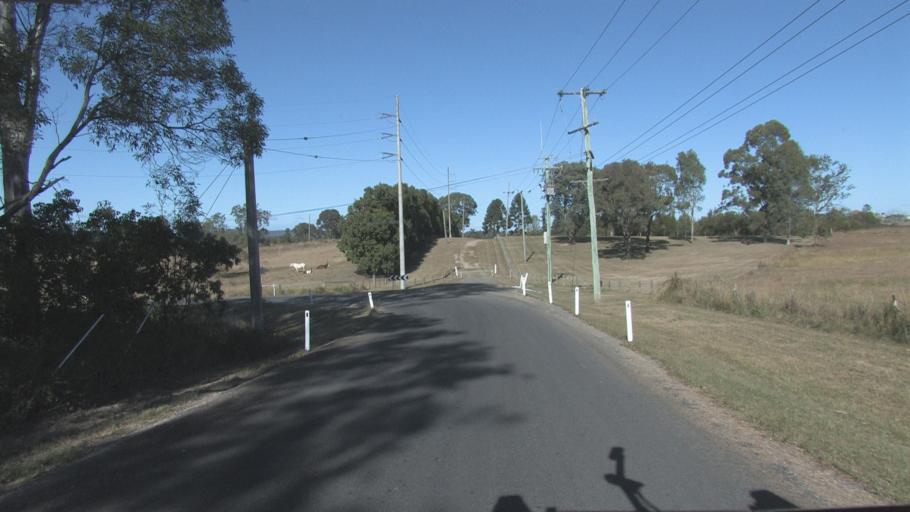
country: AU
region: Queensland
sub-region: Logan
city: Chambers Flat
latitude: -27.7589
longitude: 153.0691
